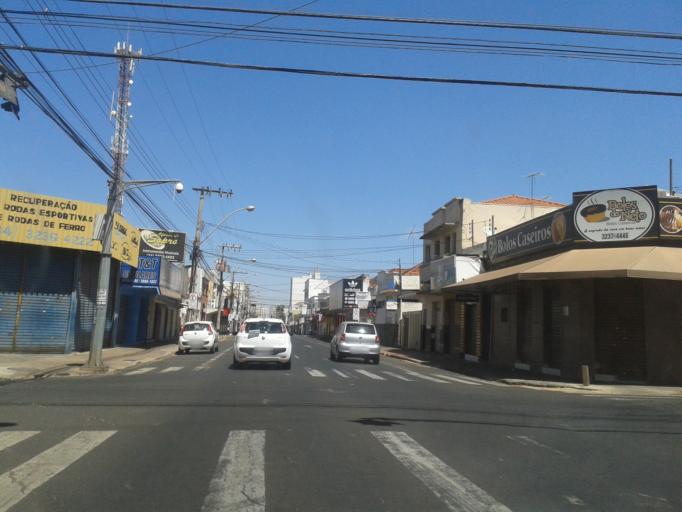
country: BR
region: Minas Gerais
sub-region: Uberlandia
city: Uberlandia
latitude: -18.9131
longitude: -48.2721
